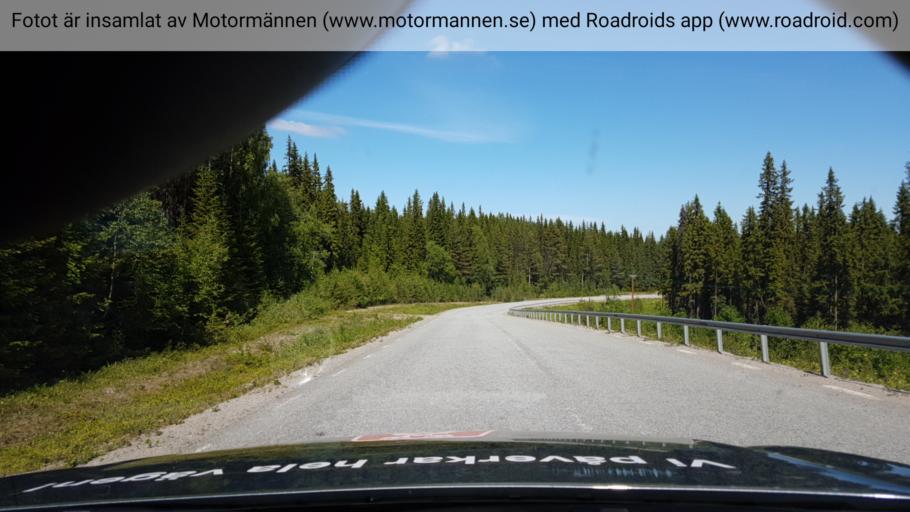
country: SE
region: Jaemtland
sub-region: OEstersunds Kommun
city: Brunflo
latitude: 62.6567
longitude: 14.9309
